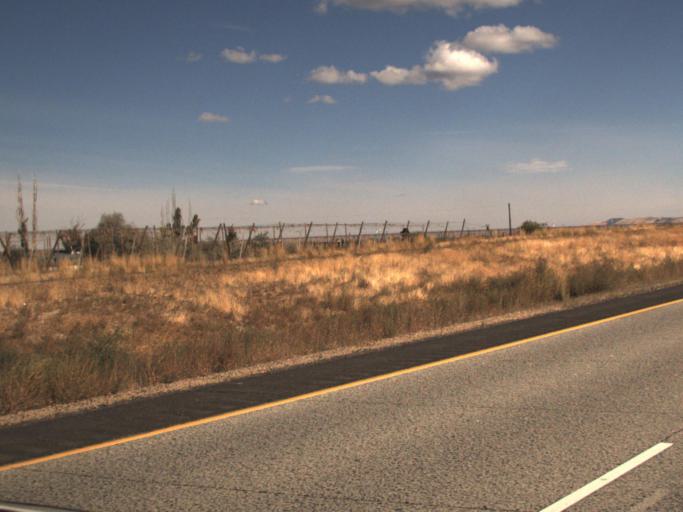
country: US
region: Washington
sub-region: Yakima County
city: Grandview
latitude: 46.2449
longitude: -119.8453
